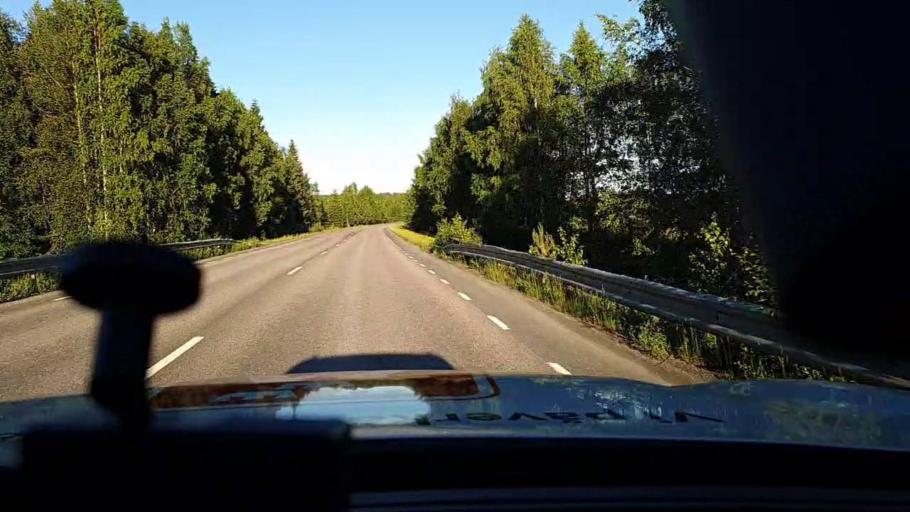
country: SE
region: Norrbotten
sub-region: Lulea Kommun
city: Lulea
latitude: 65.6138
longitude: 22.1556
